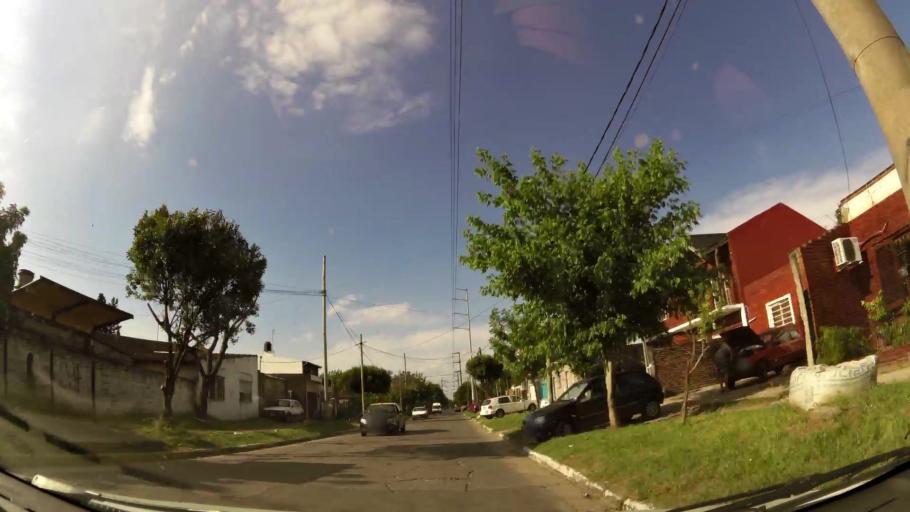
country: AR
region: Buenos Aires
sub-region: Partido de Merlo
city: Merlo
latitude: -34.6574
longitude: -58.7352
